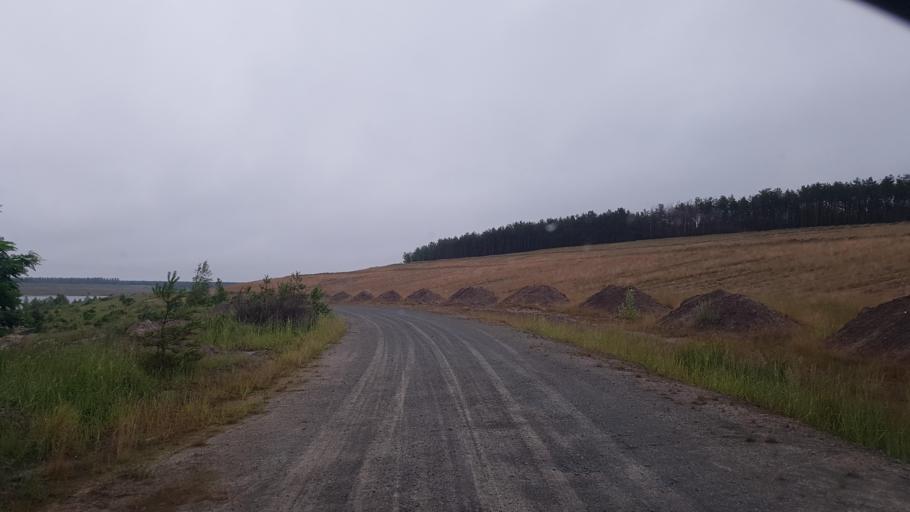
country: DE
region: Brandenburg
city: Lauchhammer
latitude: 51.5378
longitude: 13.7396
